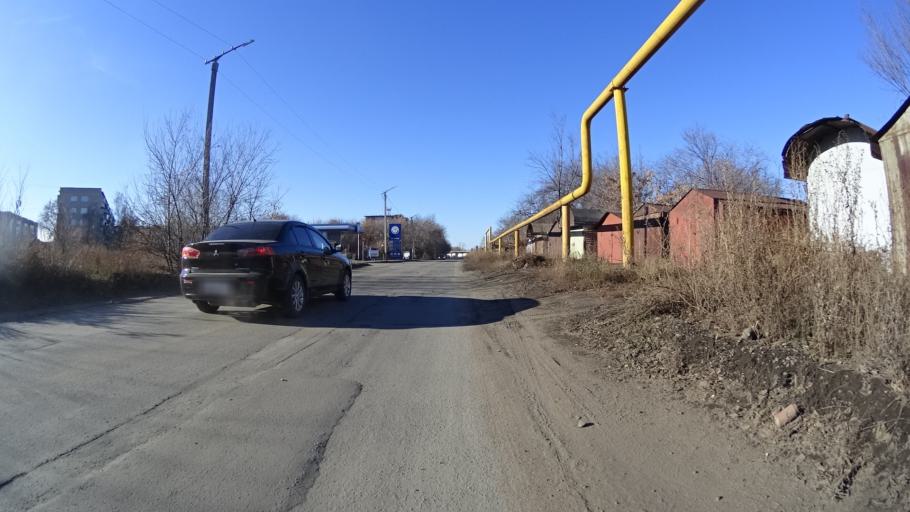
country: RU
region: Chelyabinsk
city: Troitsk
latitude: 54.0927
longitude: 61.5541
